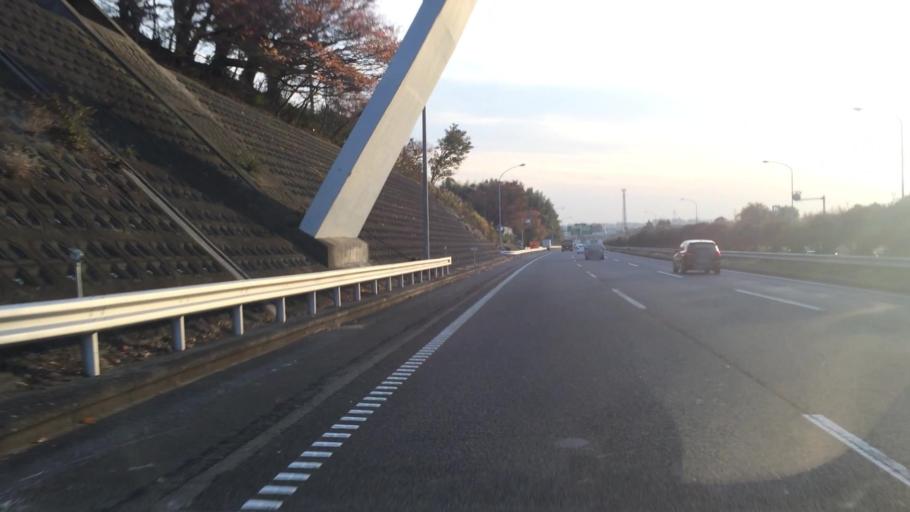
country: JP
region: Kanagawa
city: Yokohama
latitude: 35.5326
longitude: 139.5997
